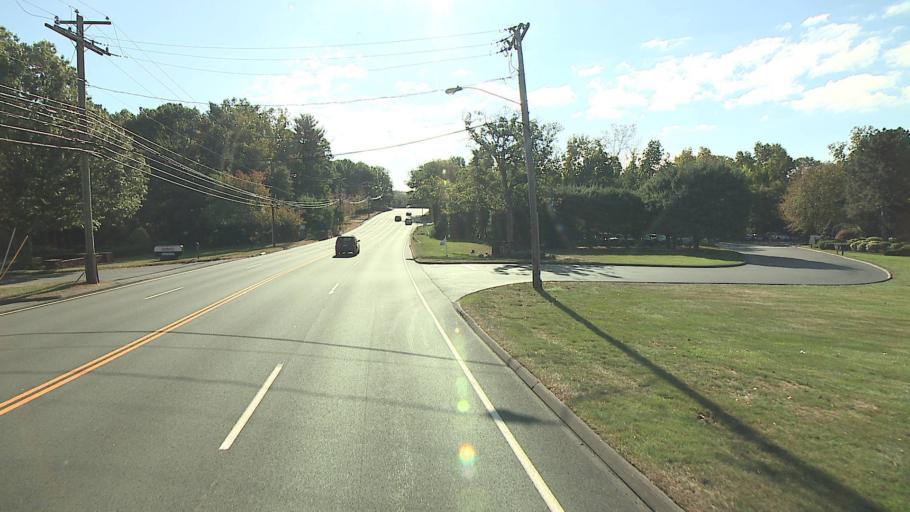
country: US
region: Connecticut
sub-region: Hartford County
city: Bristol
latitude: 41.6525
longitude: -72.9084
